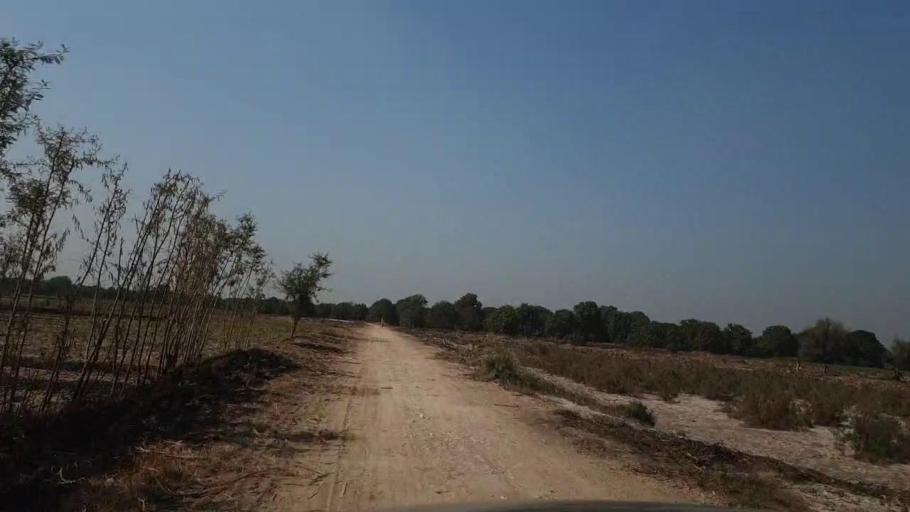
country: PK
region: Sindh
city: Tando Allahyar
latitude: 25.5530
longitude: 68.6779
